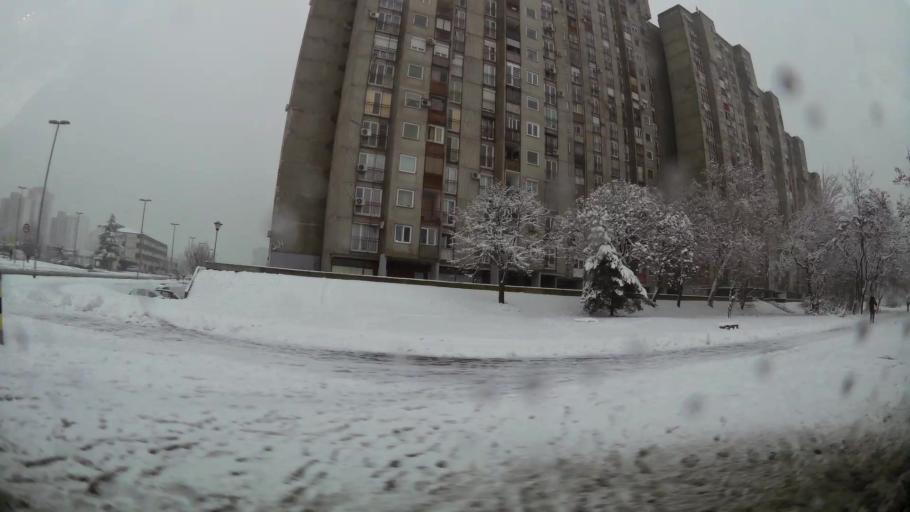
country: RS
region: Central Serbia
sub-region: Belgrade
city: Zemun
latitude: 44.8002
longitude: 20.3696
